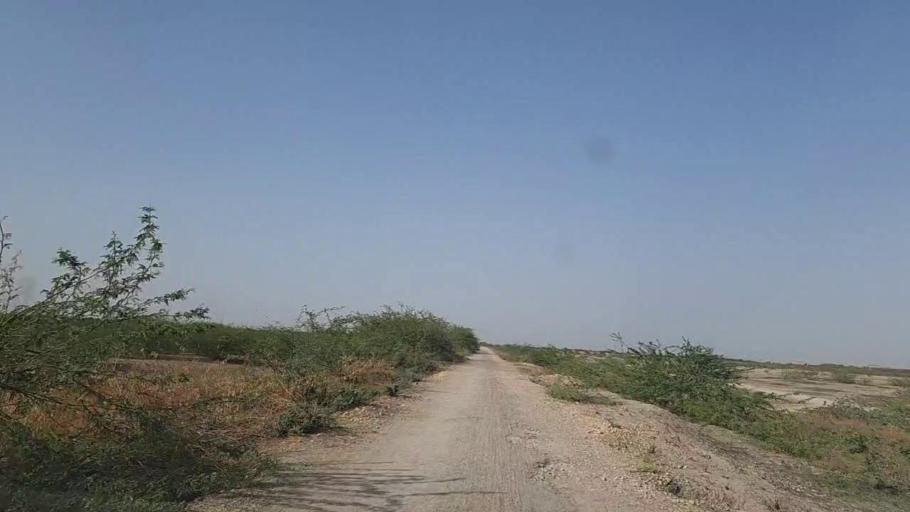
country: PK
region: Sindh
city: Naukot
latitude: 24.6050
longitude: 69.2747
